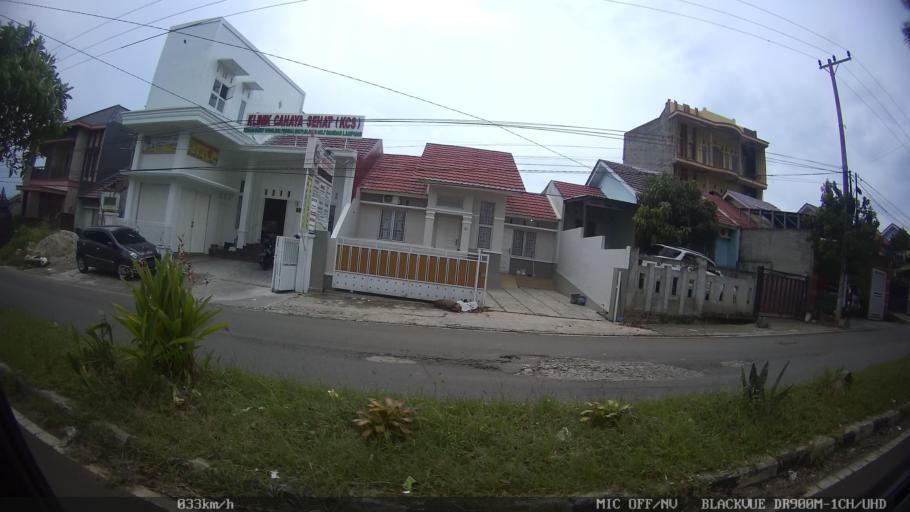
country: ID
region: Lampung
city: Kedaton
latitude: -5.3760
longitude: 105.2124
